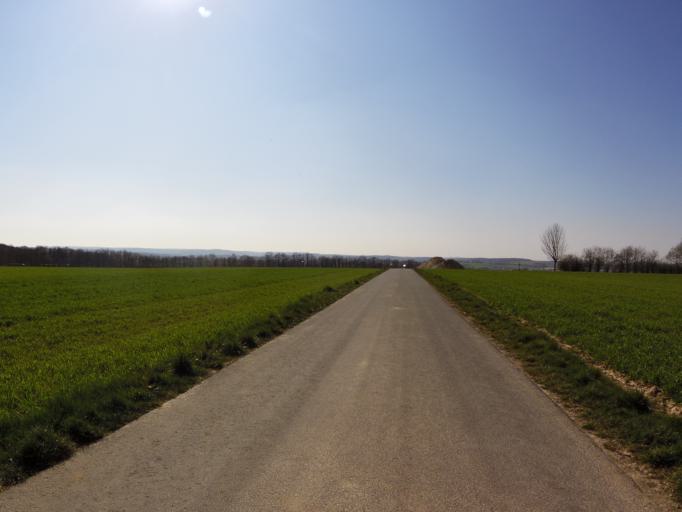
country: DE
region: Bavaria
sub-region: Regierungsbezirk Unterfranken
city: Kurnach
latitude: 49.8339
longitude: 10.0430
